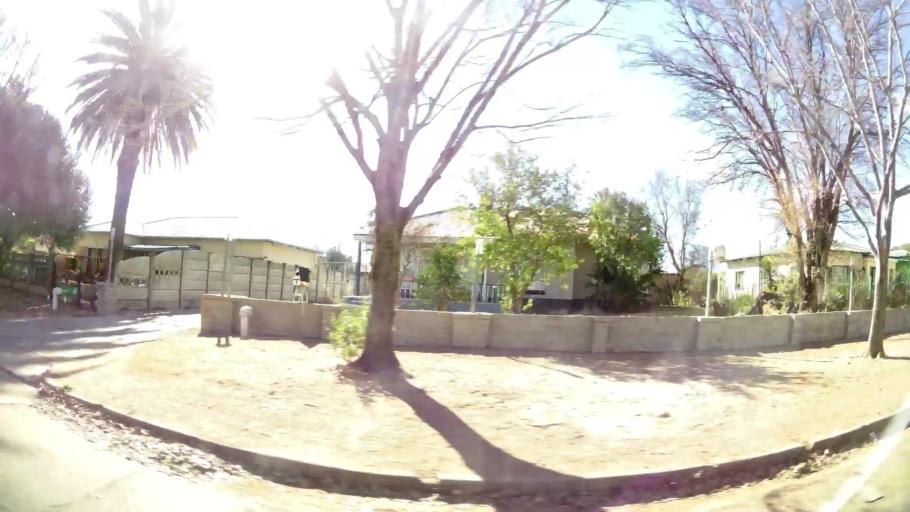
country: ZA
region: North-West
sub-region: Dr Kenneth Kaunda District Municipality
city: Klerksdorp
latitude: -26.8593
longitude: 26.6482
